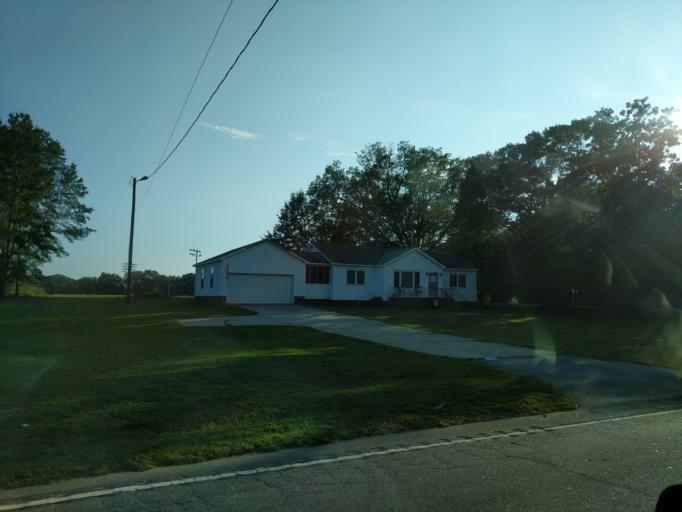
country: US
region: South Carolina
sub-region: Anderson County
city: Williamston
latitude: 34.6580
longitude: -82.4978
